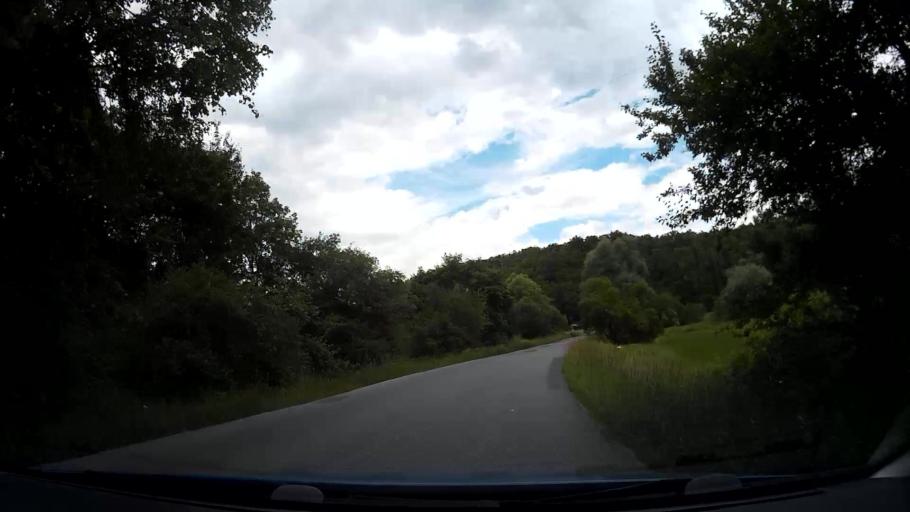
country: CZ
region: South Moravian
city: Ostopovice
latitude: 49.1441
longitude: 16.5309
